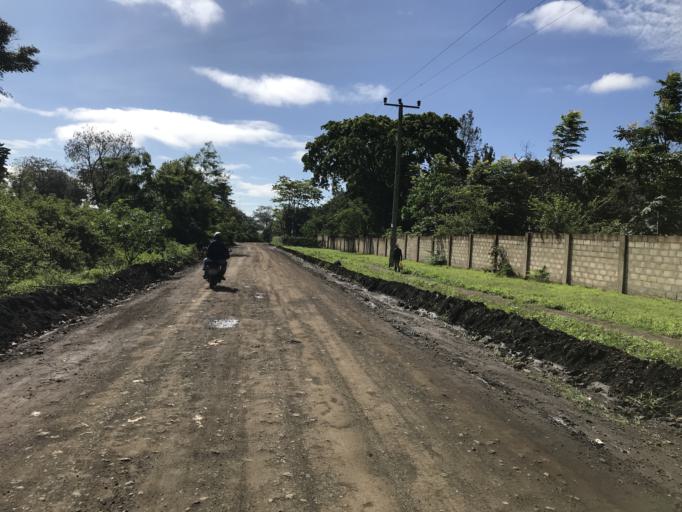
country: TZ
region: Arusha
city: Nkoaranga
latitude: -3.3811
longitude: 36.7940
